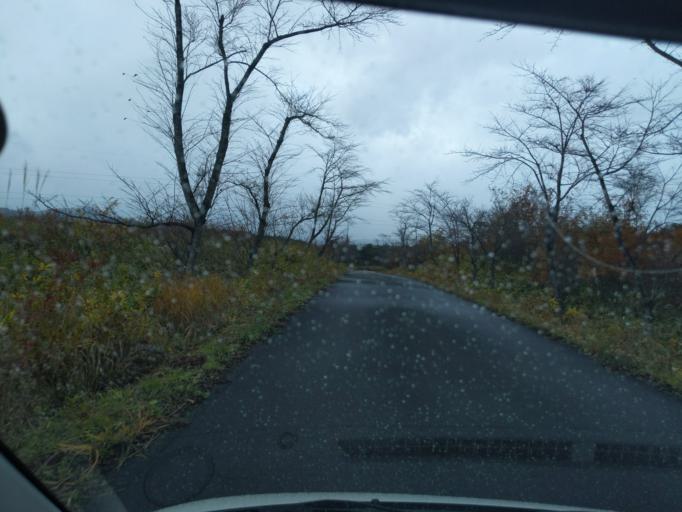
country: JP
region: Iwate
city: Mizusawa
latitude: 39.0876
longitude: 141.0096
